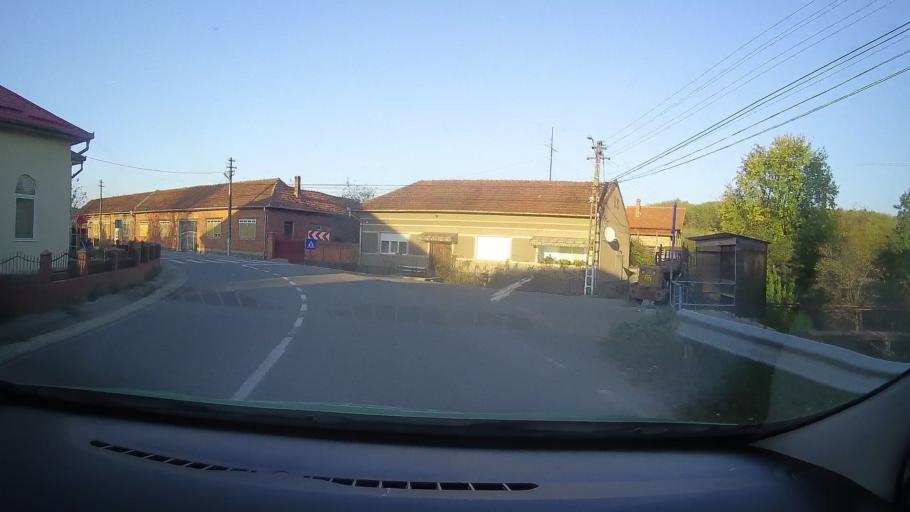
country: RO
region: Timis
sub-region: Comuna Traian Vuia
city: Traian Vuia
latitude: 45.7654
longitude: 22.0953
